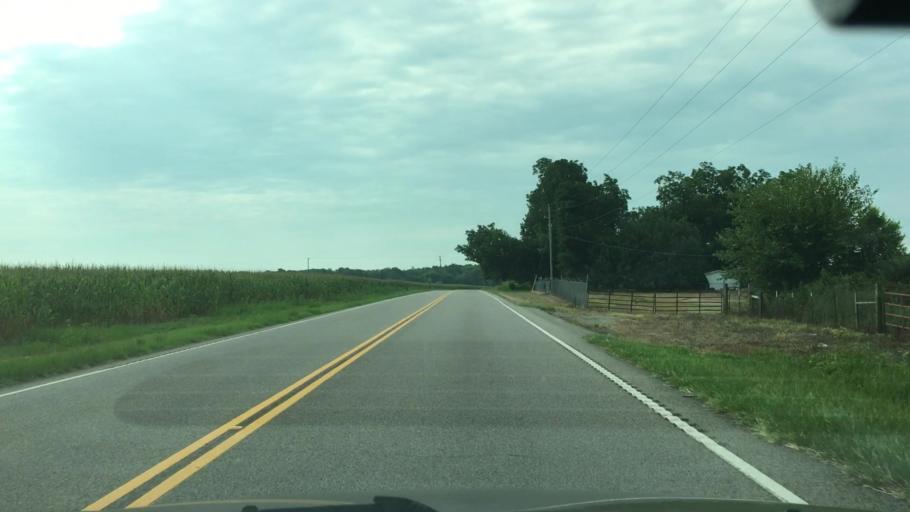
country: US
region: South Carolina
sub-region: Lexington County
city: Batesburg-Leesville
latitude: 33.6998
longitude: -81.4794
